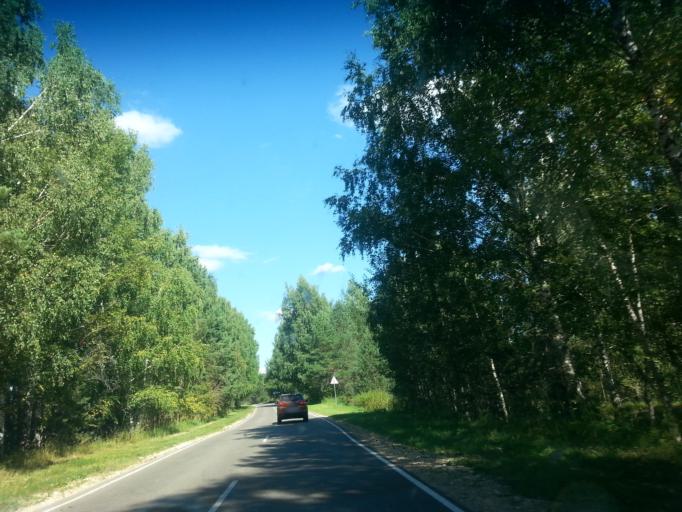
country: RU
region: Nizjnij Novgorod
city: Taremskoye
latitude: 56.0000
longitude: 42.9035
